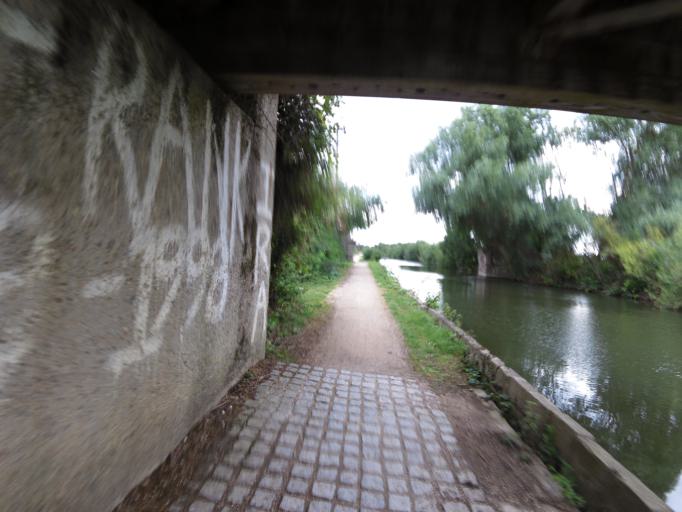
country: GB
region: England
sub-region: Hertfordshire
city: Cheshunt
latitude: 51.7153
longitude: -0.0156
